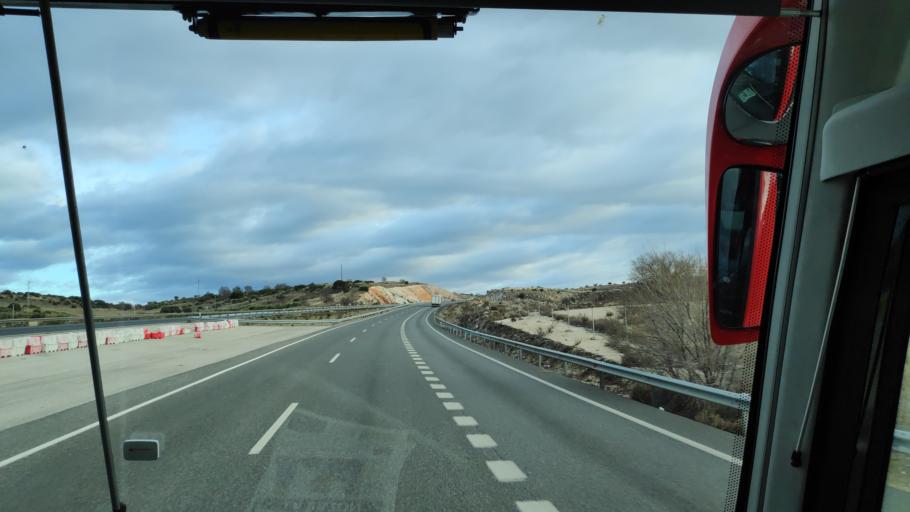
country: ES
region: Madrid
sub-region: Provincia de Madrid
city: Villarejo de Salvanes
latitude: 40.1942
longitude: -3.3031
